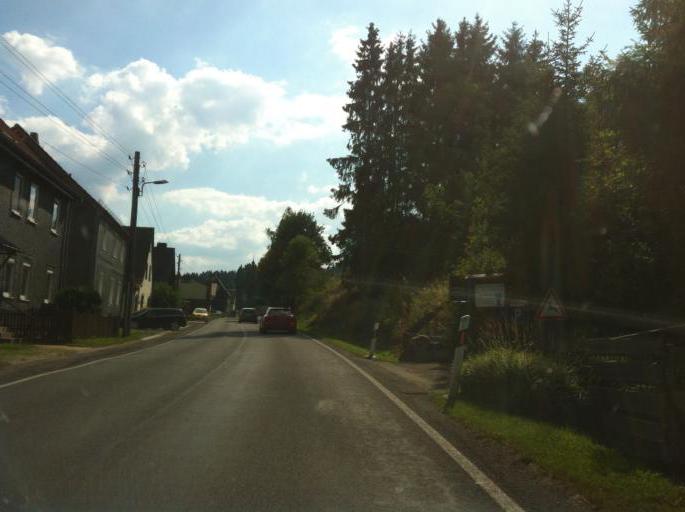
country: DE
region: Thuringia
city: Mohrenbach
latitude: 50.6279
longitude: 10.9955
